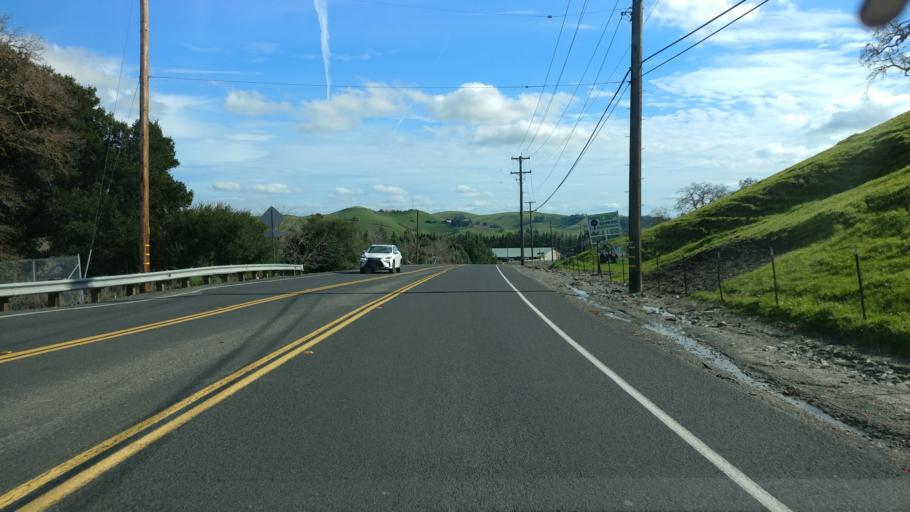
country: US
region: California
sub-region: Contra Costa County
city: Blackhawk
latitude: 37.7945
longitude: -121.8648
